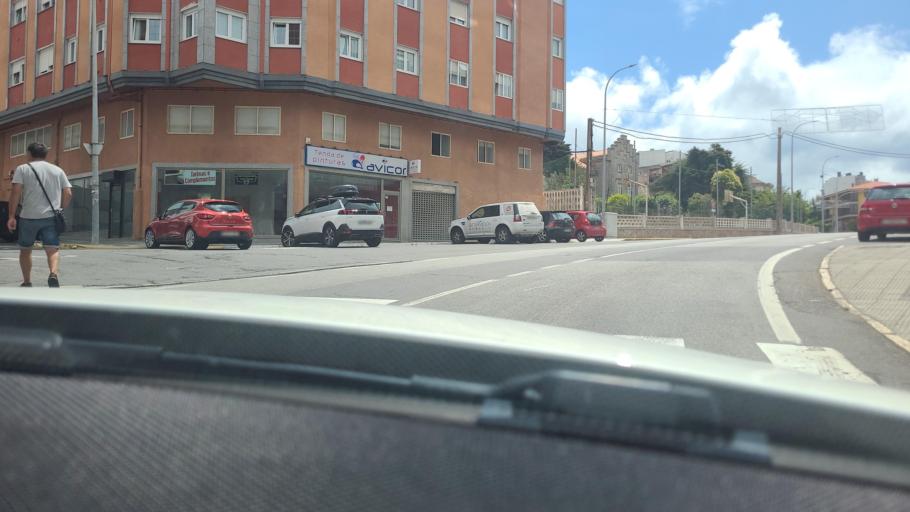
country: ES
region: Galicia
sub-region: Provincia da Coruna
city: Cee
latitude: 42.9559
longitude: -9.1877
